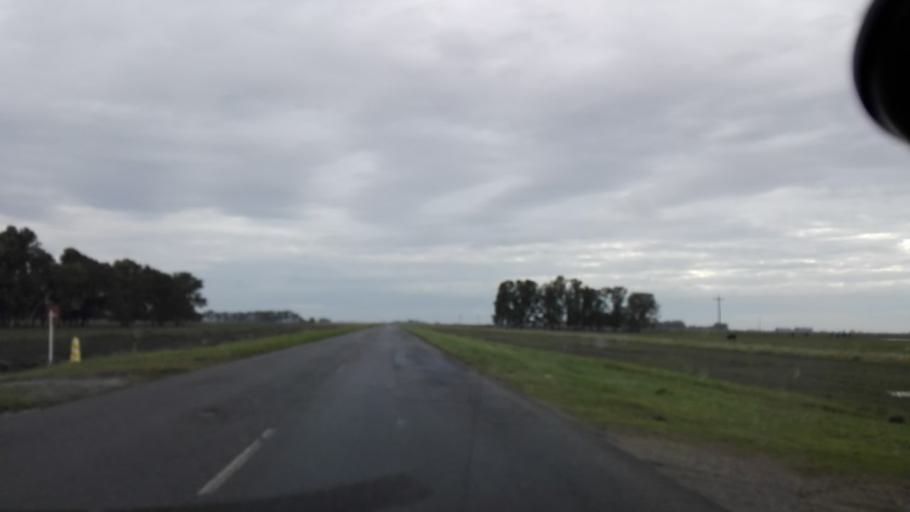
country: AR
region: Buenos Aires
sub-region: Partido de Rauch
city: Rauch
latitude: -36.6003
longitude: -59.0574
